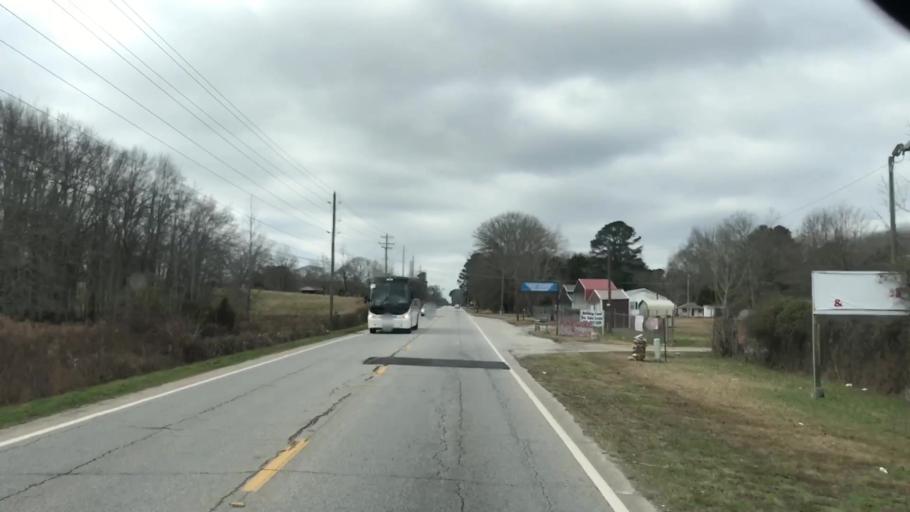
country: US
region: Georgia
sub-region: Barrow County
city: Russell
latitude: 33.9763
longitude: -83.6627
